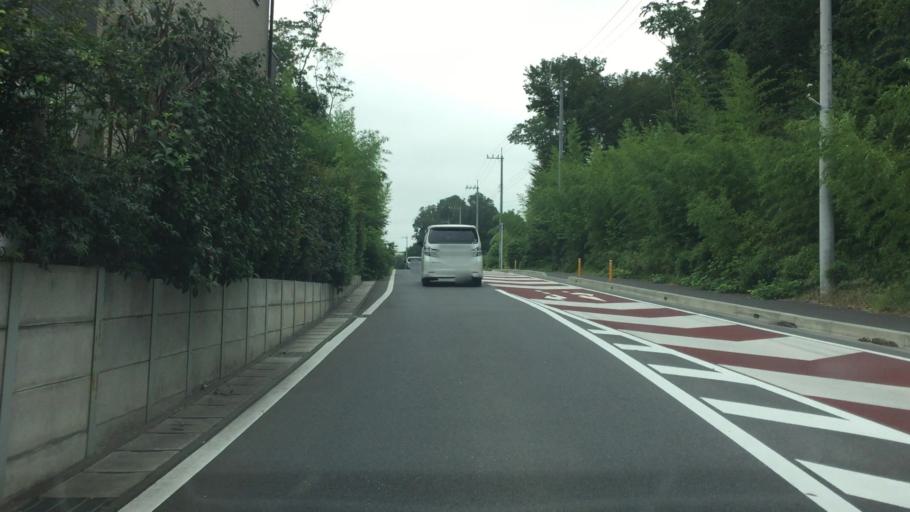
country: JP
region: Chiba
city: Abiko
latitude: 35.8406
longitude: 140.0159
